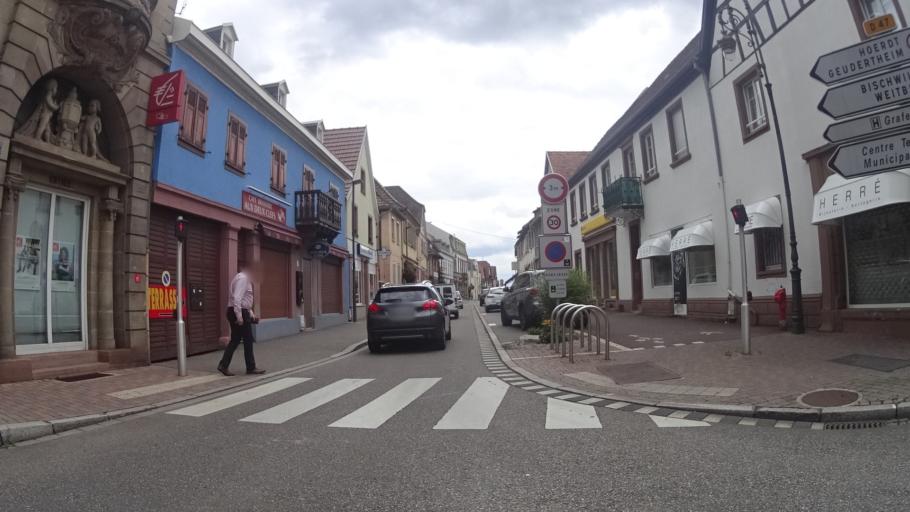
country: FR
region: Alsace
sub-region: Departement du Bas-Rhin
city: Brumath
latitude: 48.7300
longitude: 7.7113
